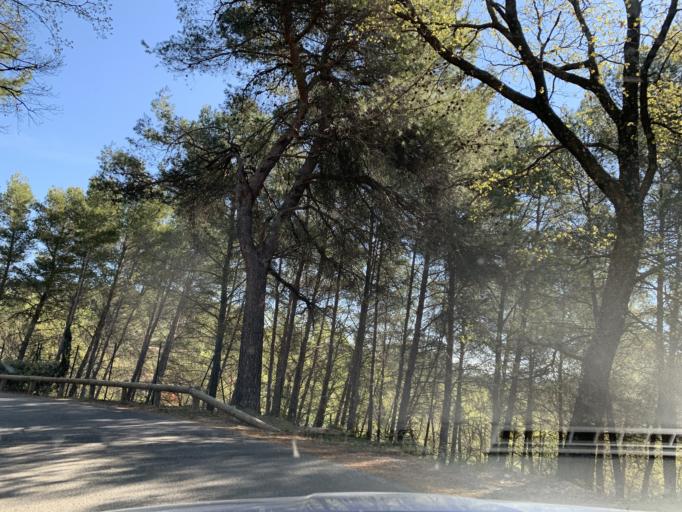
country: FR
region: Provence-Alpes-Cote d'Azur
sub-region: Departement du Vaucluse
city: Roussillon
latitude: 43.8940
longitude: 5.2906
